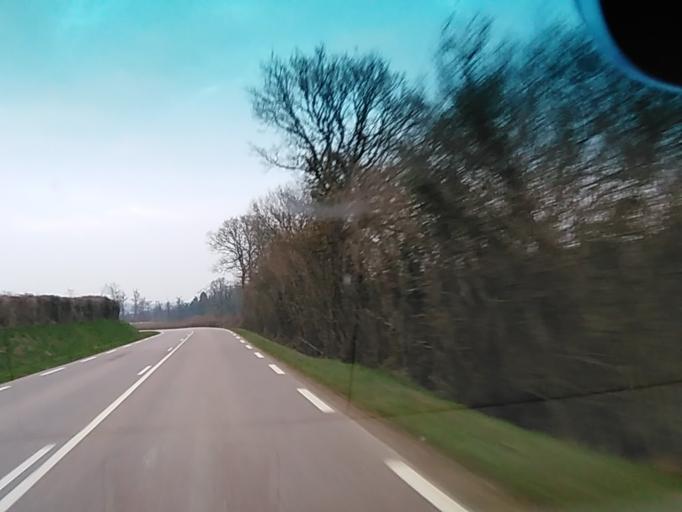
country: FR
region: Lower Normandy
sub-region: Departement de l'Orne
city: Pont-Ecrepin
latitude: 48.7405
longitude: -0.2455
